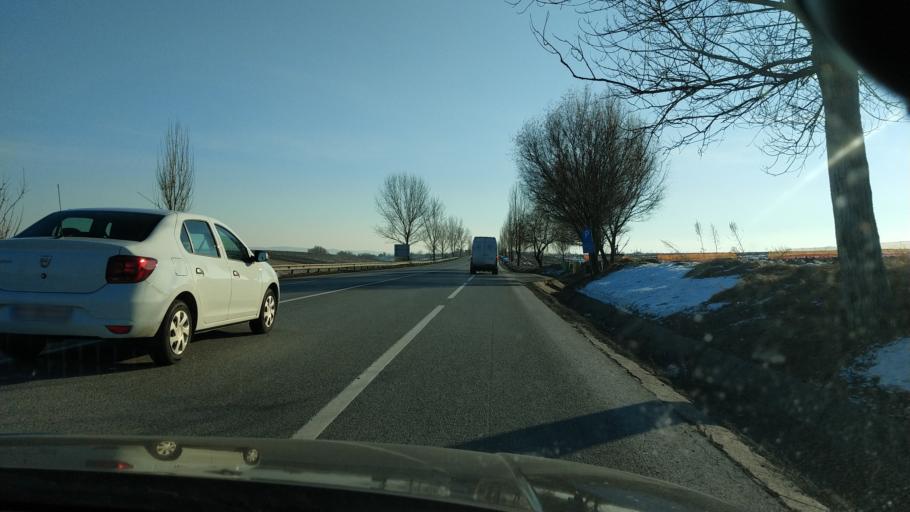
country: RO
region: Bacau
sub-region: Comuna Itesti
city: Itesti
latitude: 46.6903
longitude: 26.8946
